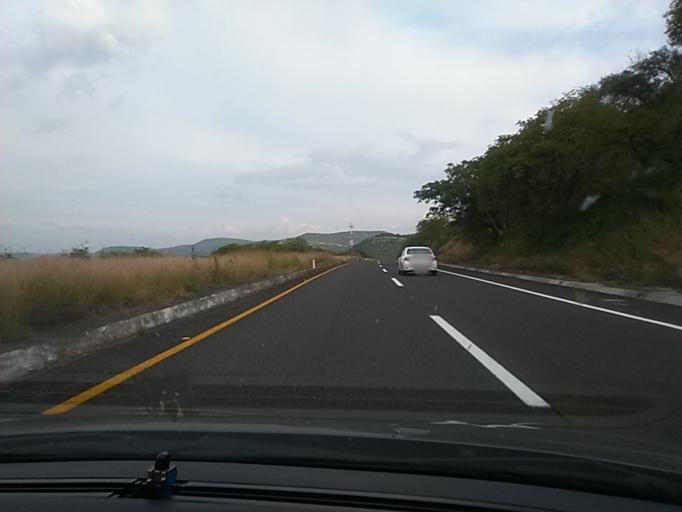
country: MX
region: Michoacan
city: Copandaro de Galeana
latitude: 19.8888
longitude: -101.2325
